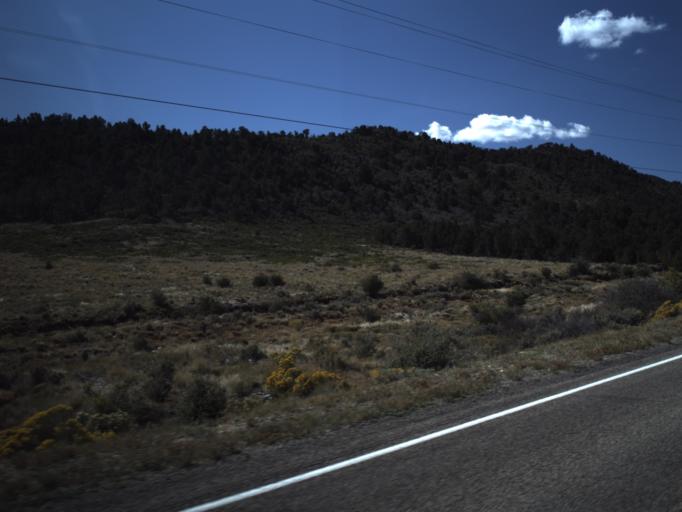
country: US
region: Utah
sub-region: Iron County
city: Cedar City
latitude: 37.6213
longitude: -113.3254
